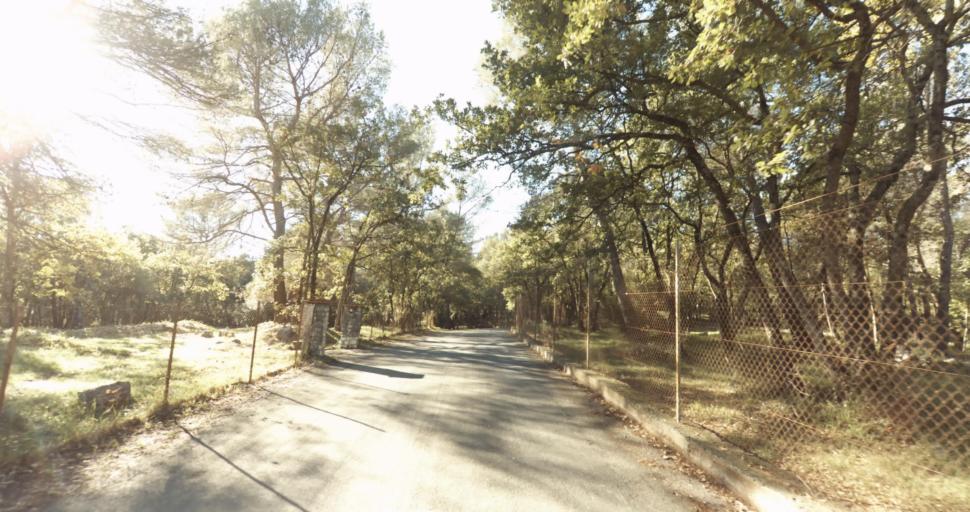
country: FR
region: Provence-Alpes-Cote d'Azur
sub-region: Departement des Alpes-Maritimes
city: Vence
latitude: 43.7128
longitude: 7.0947
